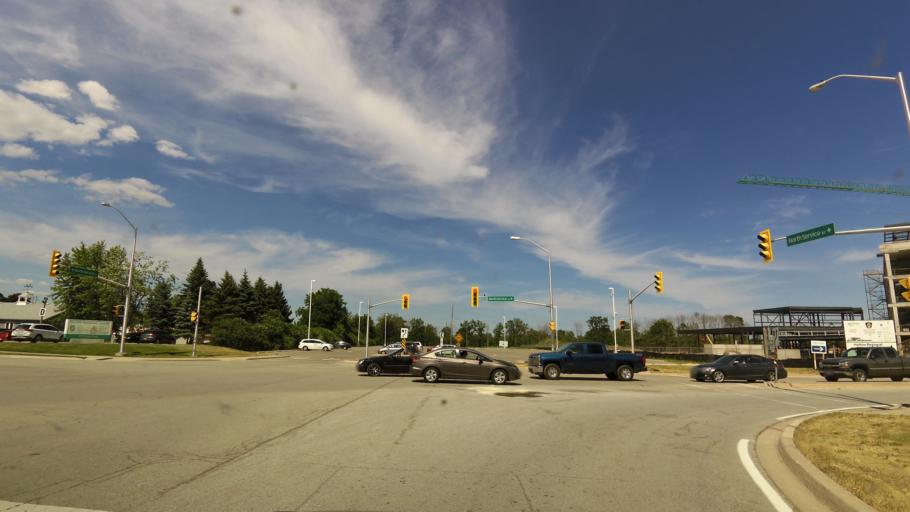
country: CA
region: Ontario
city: Oakville
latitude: 43.4138
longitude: -79.7429
